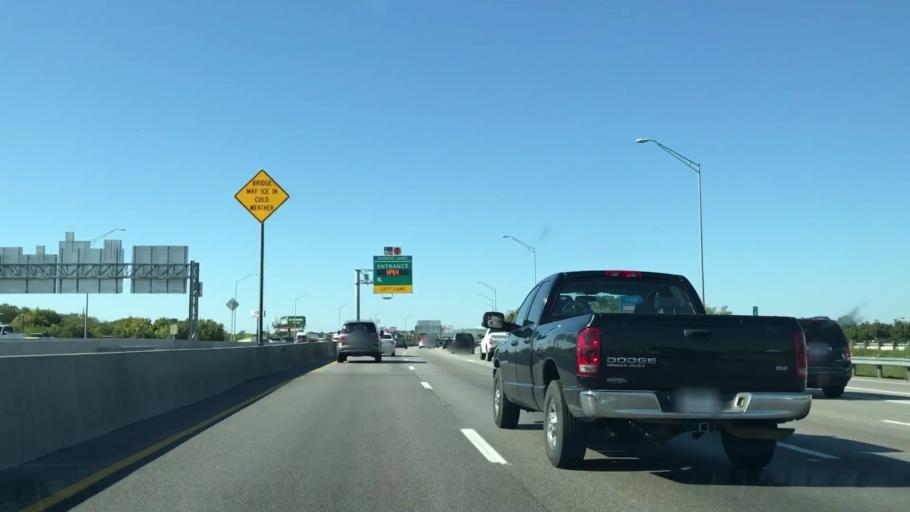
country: US
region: Texas
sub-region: Denton County
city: Lewisville
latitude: 33.0095
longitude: -96.9758
